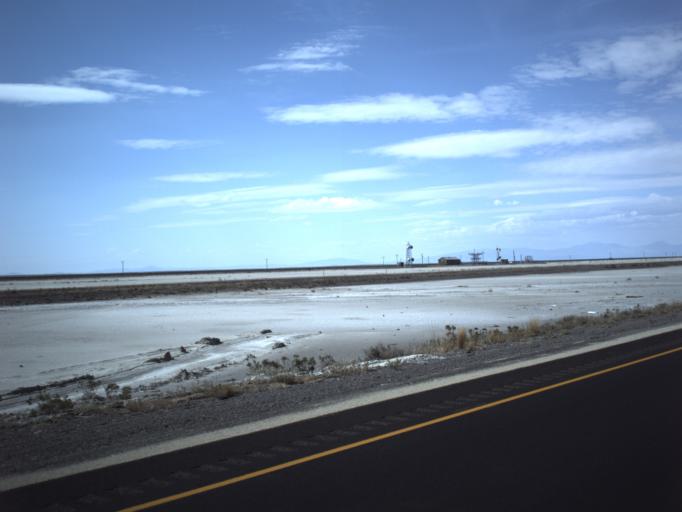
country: US
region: Utah
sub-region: Tooele County
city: Wendover
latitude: 40.7313
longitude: -113.4781
